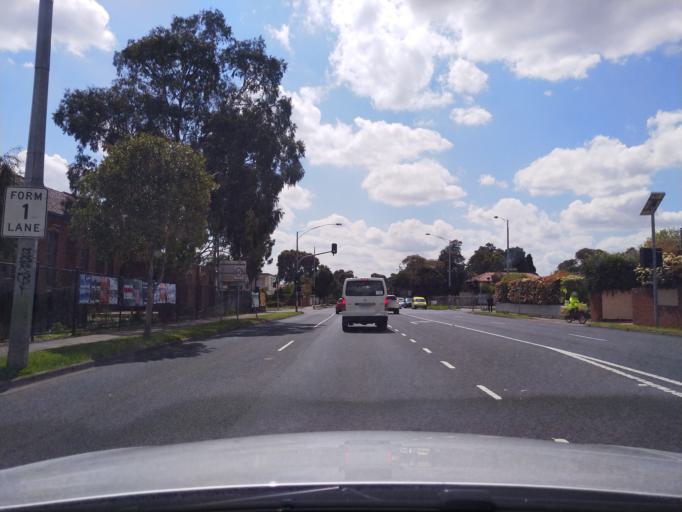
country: AU
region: Victoria
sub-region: Banyule
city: Bellfield
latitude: -37.7470
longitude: 145.0469
